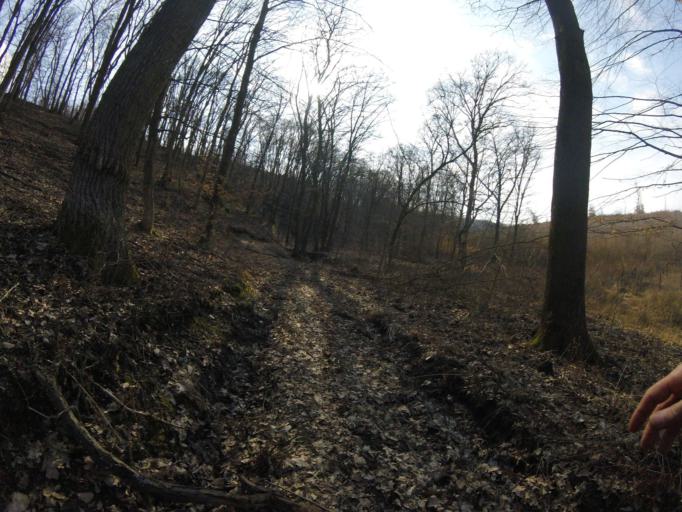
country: HU
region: Heves
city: Egerszalok
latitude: 47.8442
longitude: 20.3224
